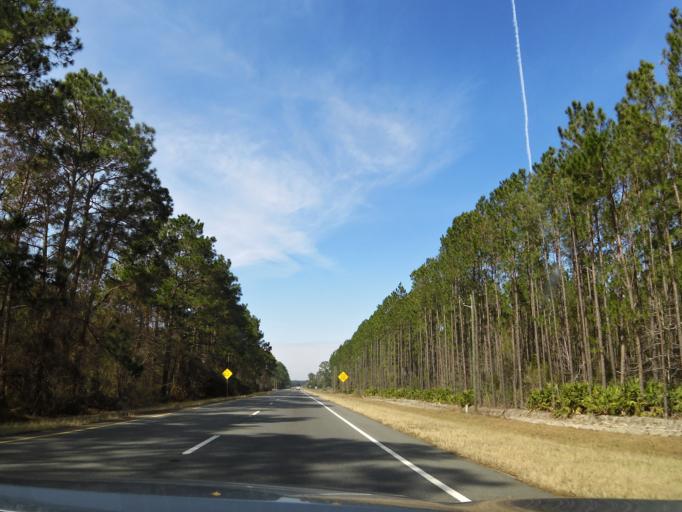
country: US
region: Georgia
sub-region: Ware County
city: Waycross
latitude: 31.1164
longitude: -82.2506
